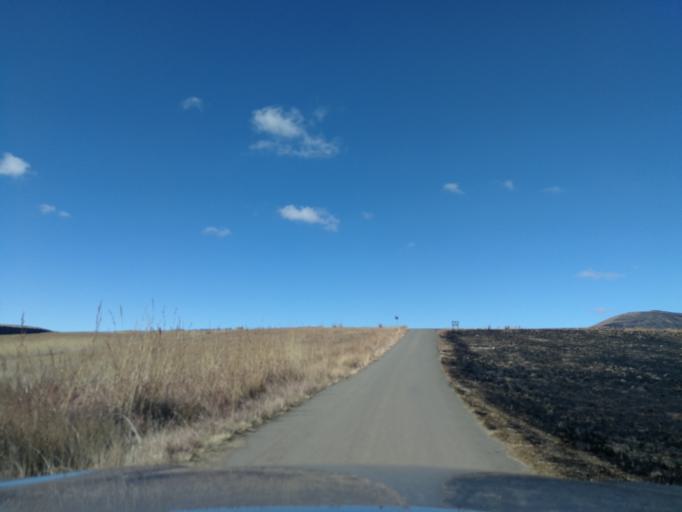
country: ZA
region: Orange Free State
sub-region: Thabo Mofutsanyana District Municipality
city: Phuthaditjhaba
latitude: -28.5127
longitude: 28.6205
